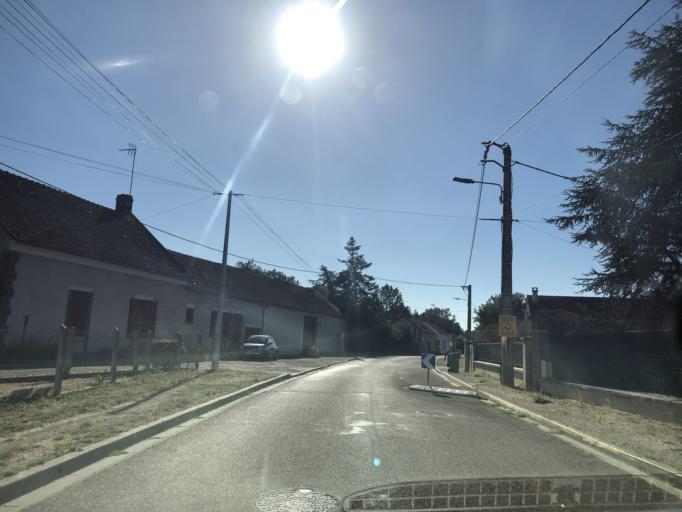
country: FR
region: Bourgogne
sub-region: Departement de l'Yonne
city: Cheny
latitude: 47.9238
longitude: 3.5300
